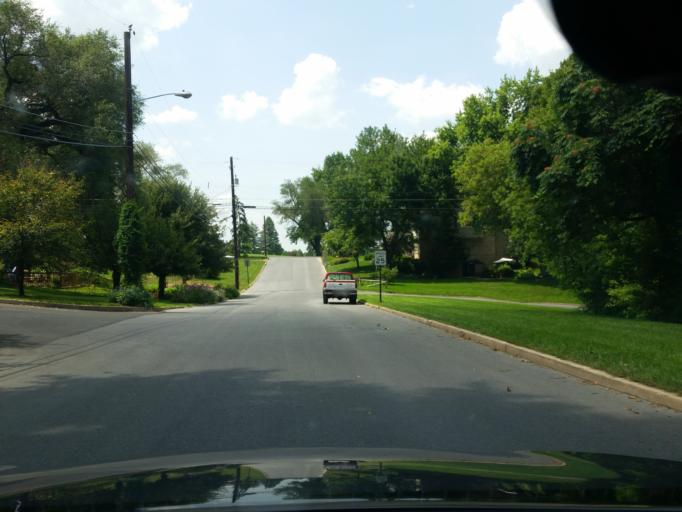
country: US
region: Pennsylvania
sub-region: Cumberland County
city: Camp Hill
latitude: 40.2554
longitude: -76.9367
